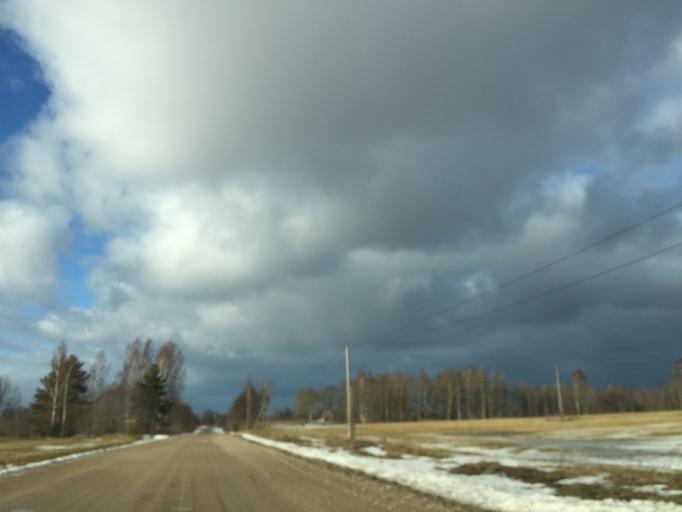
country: LV
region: Limbazu Rajons
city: Limbazi
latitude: 57.6182
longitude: 24.5781
